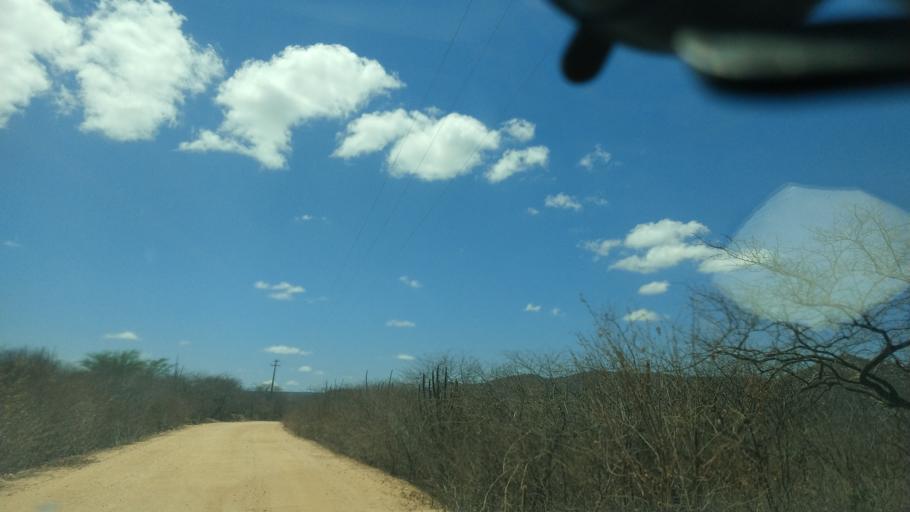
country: BR
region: Rio Grande do Norte
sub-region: Cerro Cora
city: Cerro Cora
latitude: -6.0155
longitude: -36.3057
